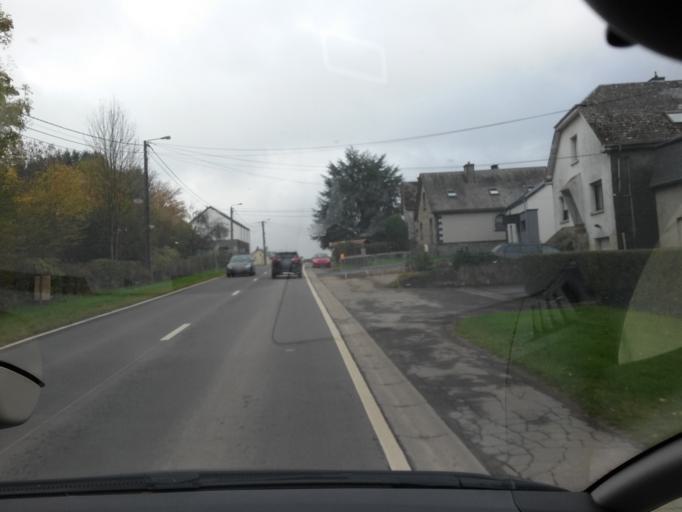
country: BE
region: Wallonia
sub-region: Province du Luxembourg
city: Habay-la-Vieille
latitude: 49.7269
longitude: 5.6543
